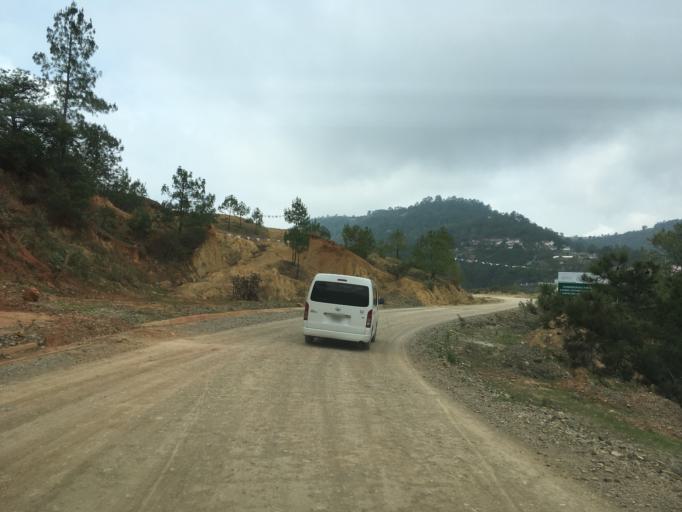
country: MX
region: Oaxaca
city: Santiago Tilantongo
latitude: 17.1993
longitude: -97.2804
